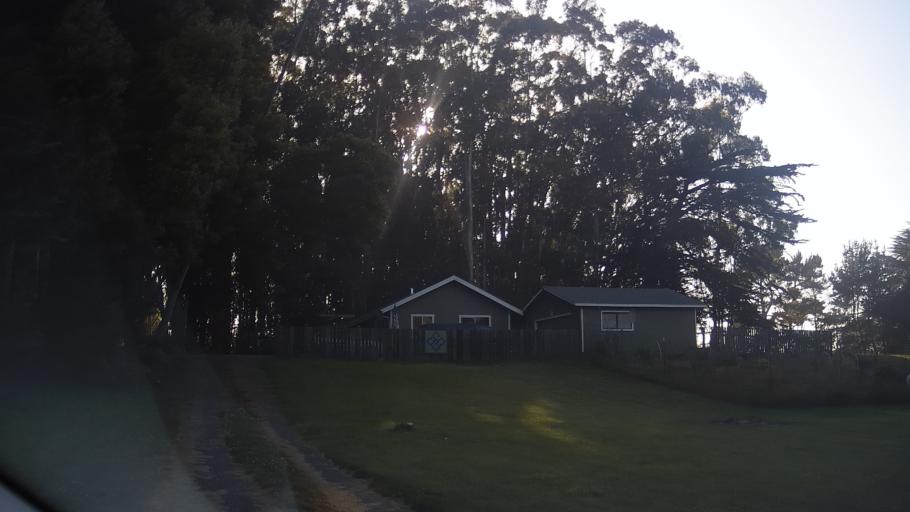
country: US
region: California
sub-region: Mendocino County
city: Fort Bragg
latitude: 39.5220
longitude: -123.7614
